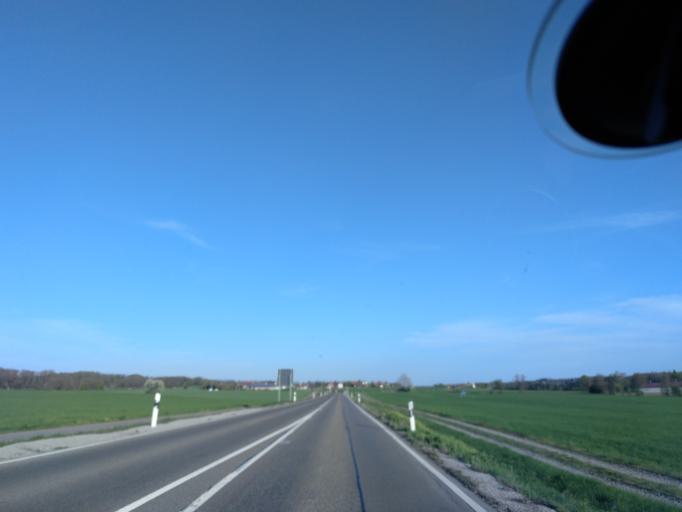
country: DE
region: Baden-Wuerttemberg
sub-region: Regierungsbezirk Stuttgart
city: Ilshofen
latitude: 49.1586
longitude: 9.9630
